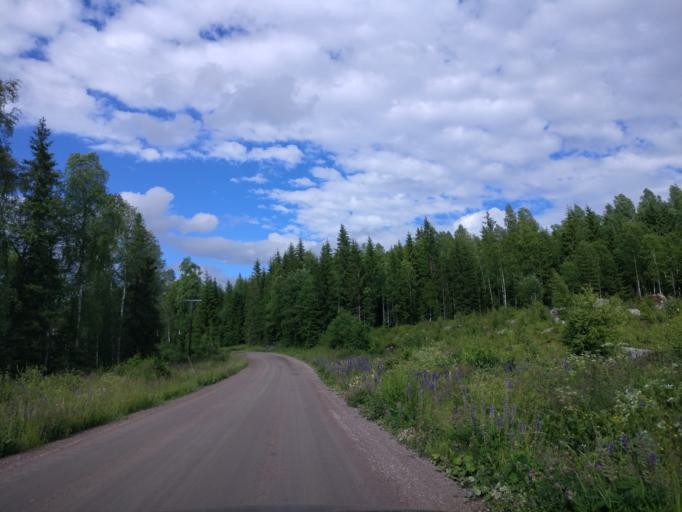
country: SE
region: Vaermland
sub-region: Hagfors Kommun
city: Ekshaerad
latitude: 60.0338
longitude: 13.4895
